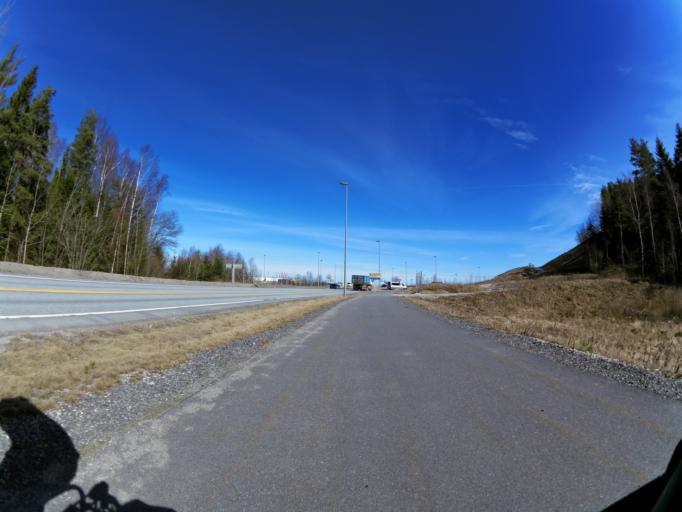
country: NO
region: Ostfold
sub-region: Sarpsborg
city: Sarpsborg
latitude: 59.3152
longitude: 11.0221
